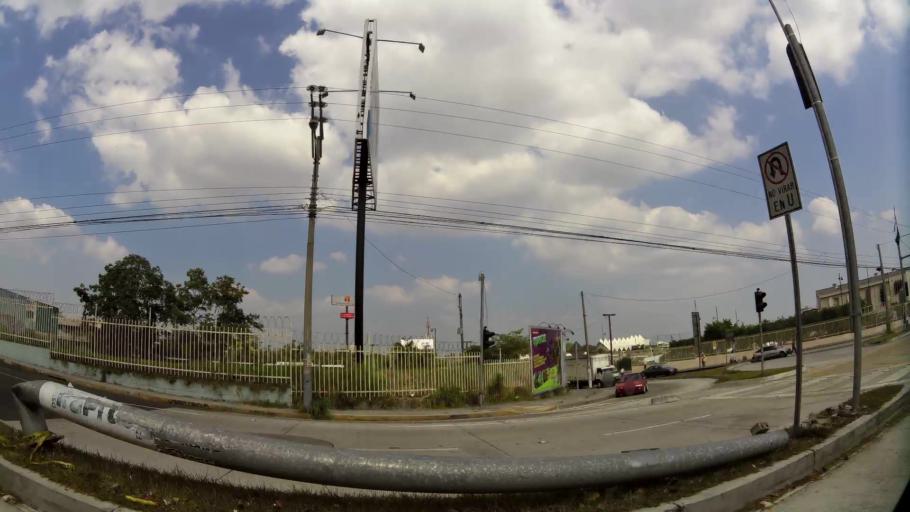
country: SV
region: San Salvador
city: San Salvador
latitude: 13.7030
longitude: -89.2089
